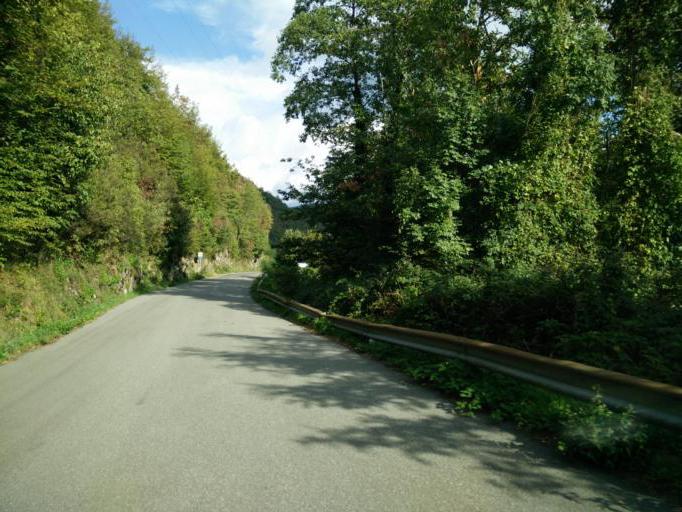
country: IT
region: Tuscany
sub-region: Provincia di Massa-Carrara
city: Zeri
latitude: 44.3503
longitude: 9.7879
